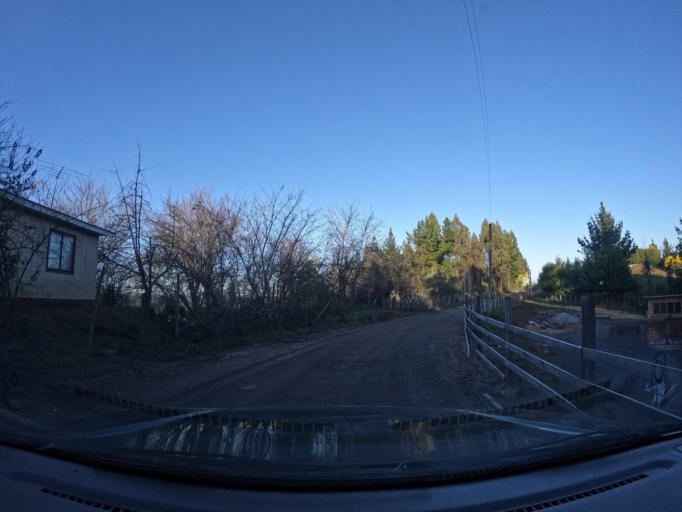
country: CL
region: Biobio
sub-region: Provincia de Concepcion
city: Chiguayante
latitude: -37.0127
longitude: -72.8447
